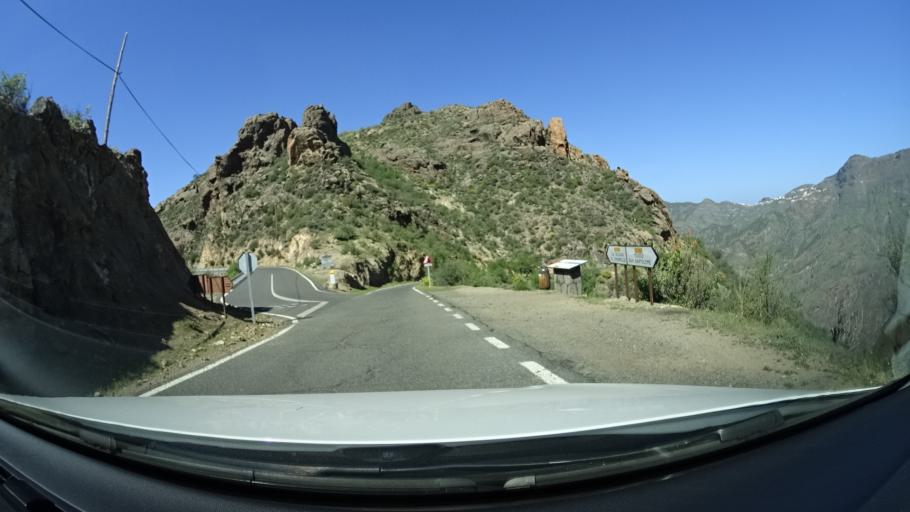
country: ES
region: Canary Islands
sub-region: Provincia de Las Palmas
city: Tejeda
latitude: 27.9891
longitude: -15.6345
